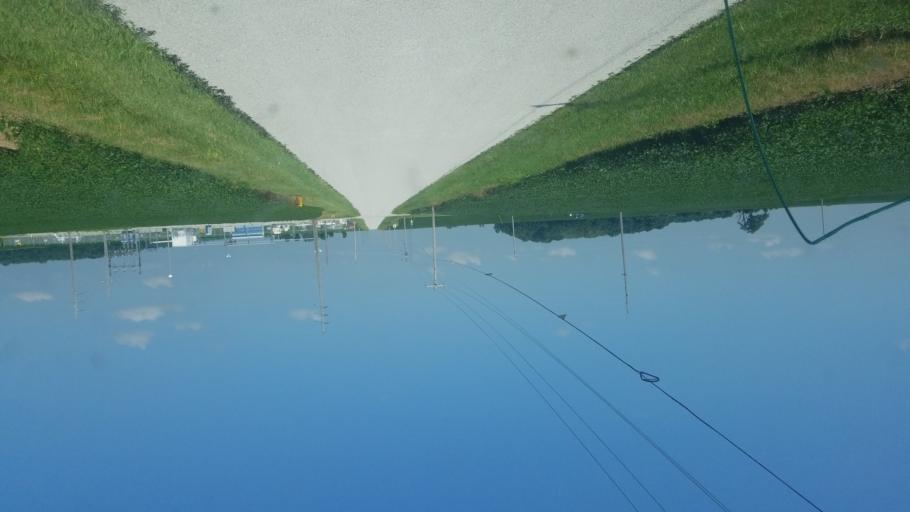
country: US
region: Ohio
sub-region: Hardin County
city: Kenton
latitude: 40.7035
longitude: -83.6903
